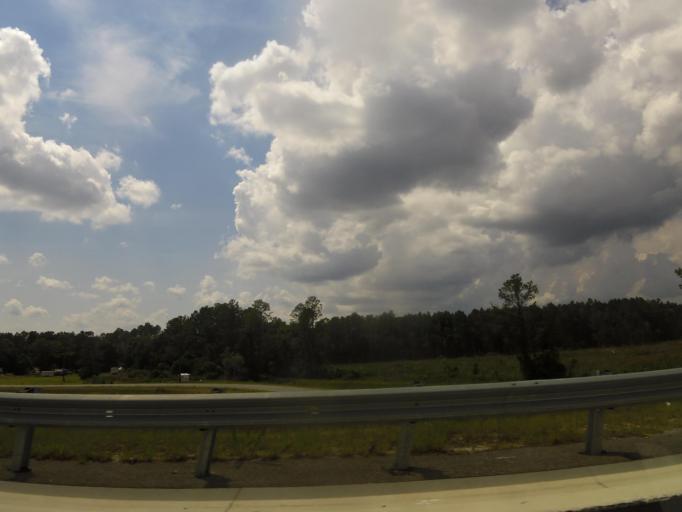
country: US
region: Florida
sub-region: Duval County
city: Baldwin
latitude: 30.3095
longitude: -81.9883
